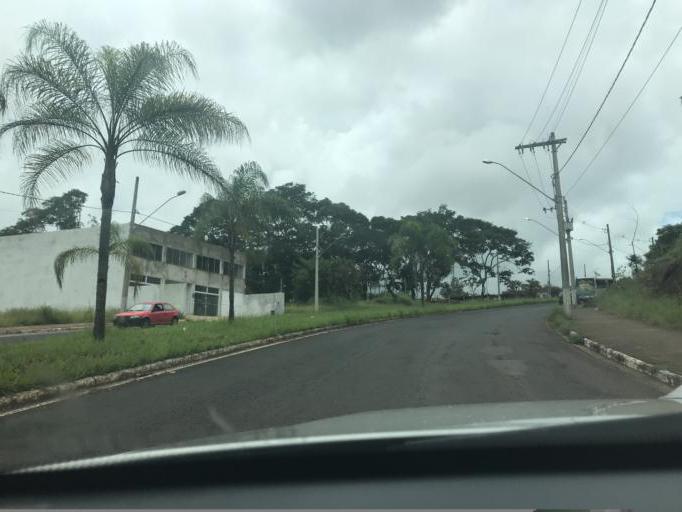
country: BR
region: Minas Gerais
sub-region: Araxa
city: Araxa
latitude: -19.5814
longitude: -46.9419
